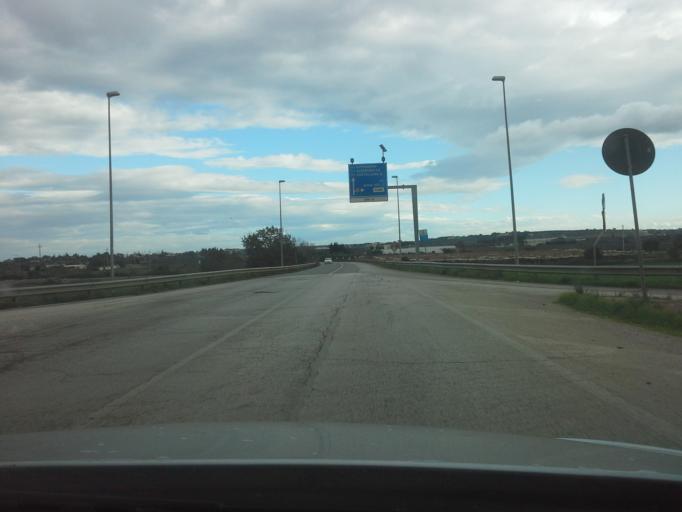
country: IT
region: Apulia
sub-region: Provincia di Bari
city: Turi
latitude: 40.9072
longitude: 17.0103
